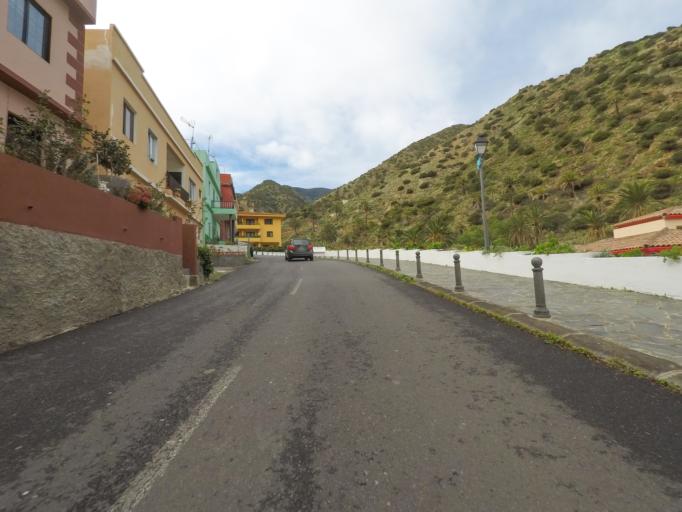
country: ES
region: Canary Islands
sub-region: Provincia de Santa Cruz de Tenerife
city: Vallehermosa
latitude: 28.1816
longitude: -17.2669
